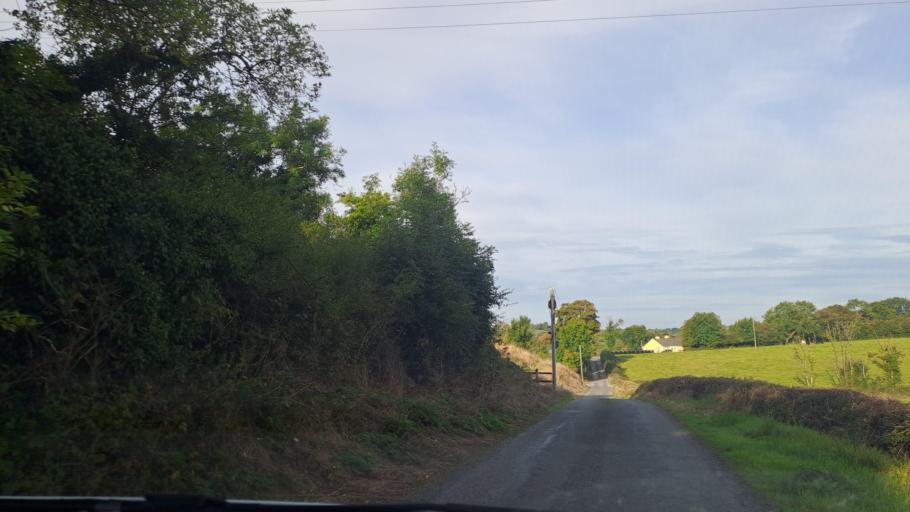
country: IE
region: Ulster
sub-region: An Cabhan
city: Bailieborough
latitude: 53.9895
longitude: -6.8834
